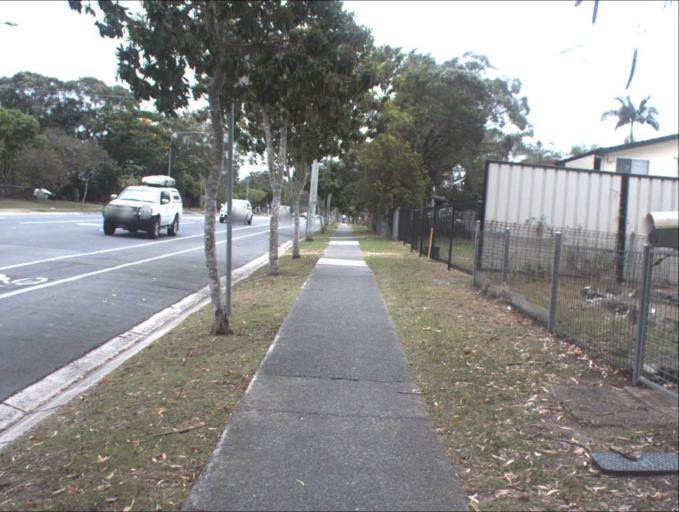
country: AU
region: Queensland
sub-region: Logan
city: Logan City
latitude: -27.6490
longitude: 153.1086
